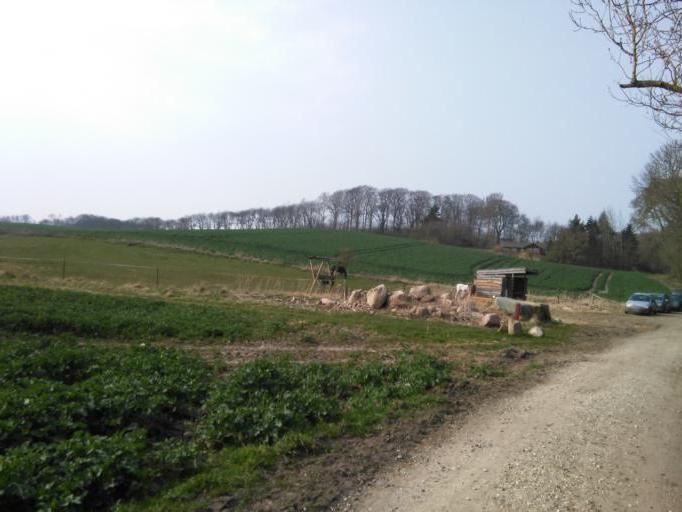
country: DK
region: Central Jutland
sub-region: Arhus Kommune
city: Beder
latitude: 56.0835
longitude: 10.2213
